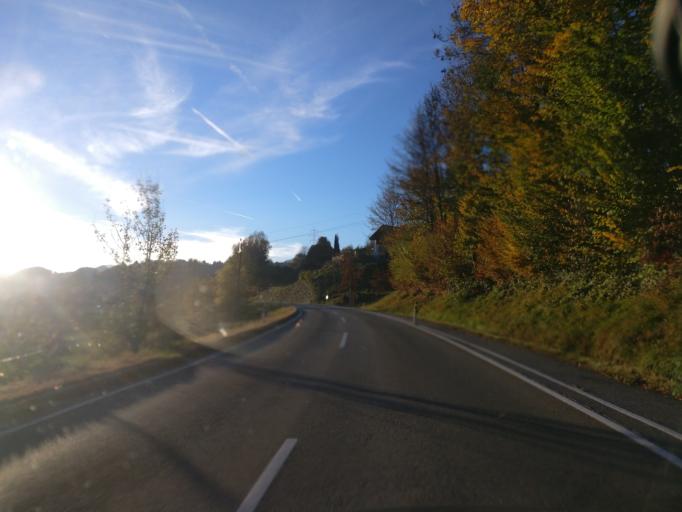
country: AT
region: Salzburg
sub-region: Politischer Bezirk Sankt Johann im Pongau
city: Schwarzach im Pongau
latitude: 47.3252
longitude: 13.1617
